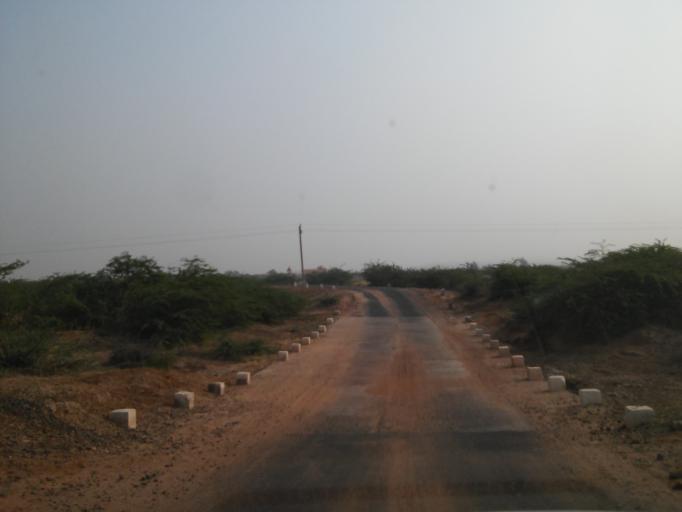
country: IN
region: Gujarat
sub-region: Kachchh
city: Bhuj
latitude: 23.8221
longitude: 69.7353
